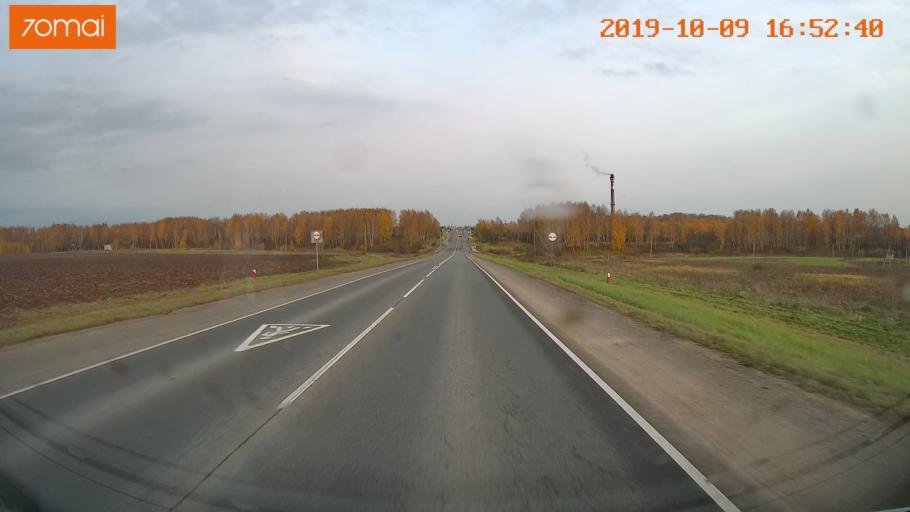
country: RU
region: Ivanovo
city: Privolzhsk
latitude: 57.3795
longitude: 41.2532
